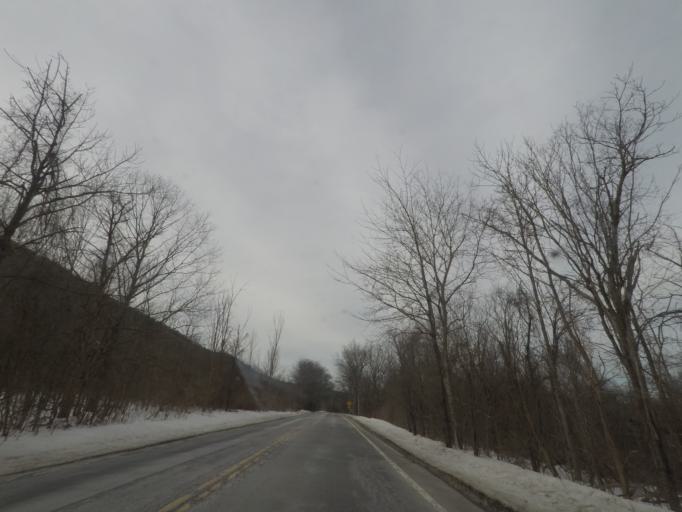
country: US
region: New York
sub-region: Albany County
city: Altamont
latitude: 42.6746
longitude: -74.0141
